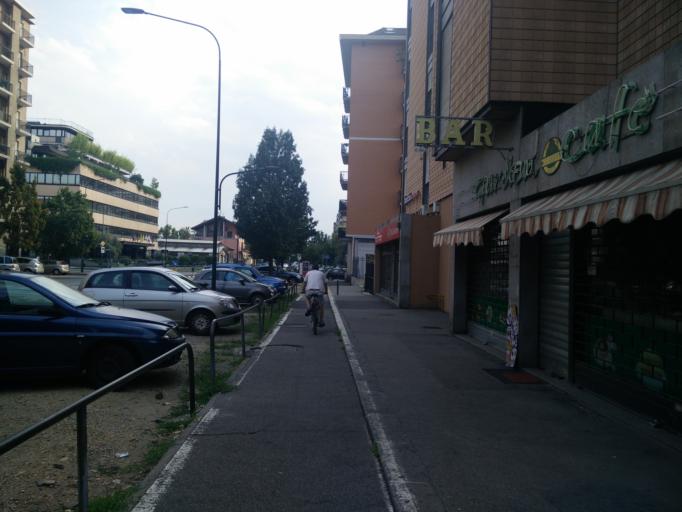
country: IT
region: Piedmont
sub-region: Provincia di Torino
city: Nichelino
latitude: 45.0242
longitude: 7.6517
